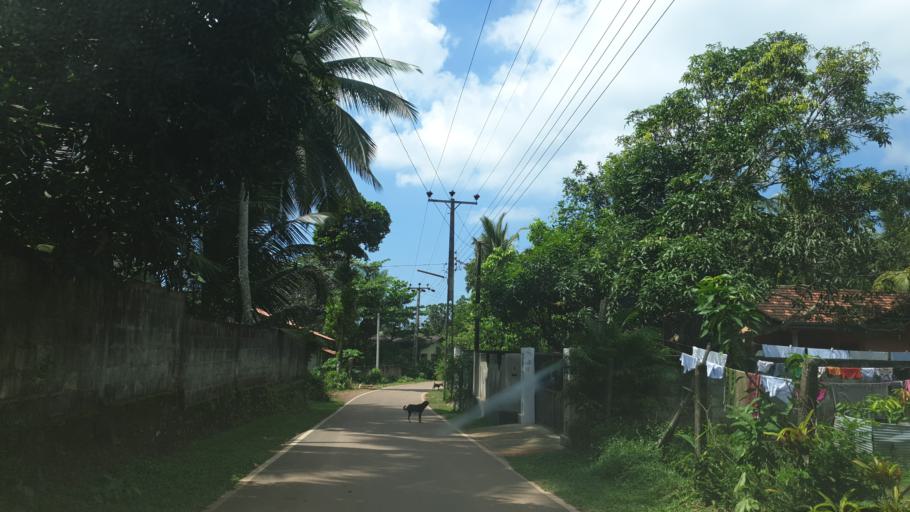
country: LK
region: Western
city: Panadura
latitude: 6.6758
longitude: 79.9640
